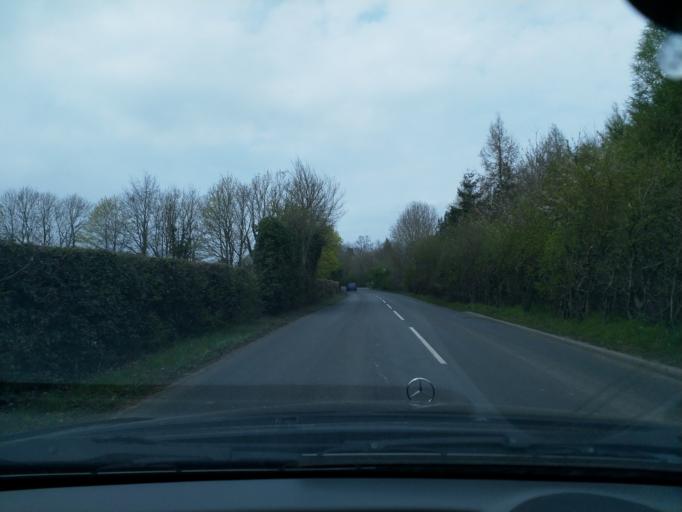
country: GB
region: England
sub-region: Warwickshire
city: Royal Leamington Spa
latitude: 52.3210
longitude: -1.5331
